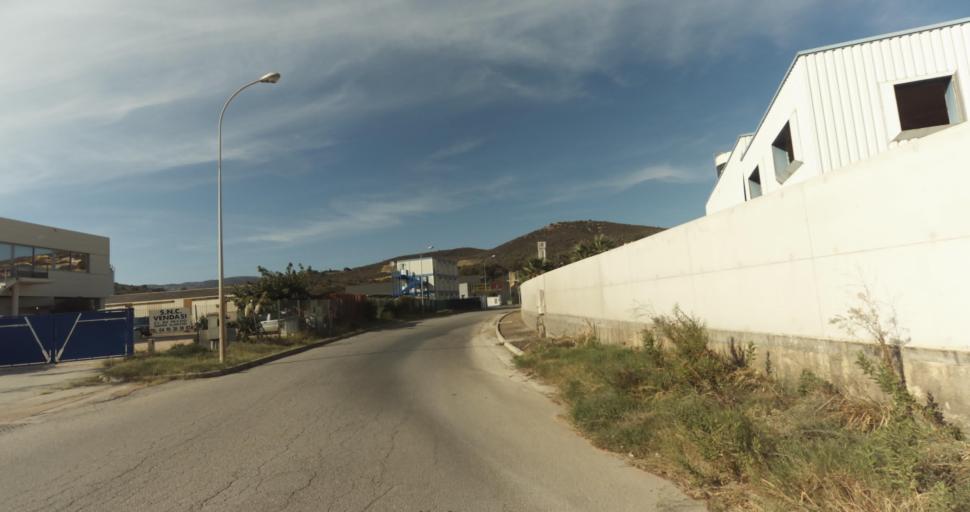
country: FR
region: Corsica
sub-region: Departement de la Corse-du-Sud
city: Ajaccio
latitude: 41.9312
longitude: 8.7871
